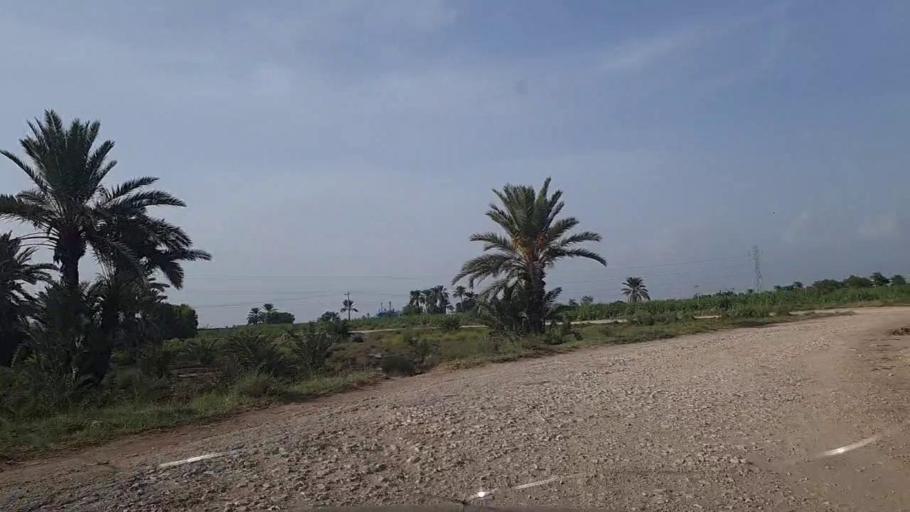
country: PK
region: Sindh
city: Ghotki
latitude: 28.0060
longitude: 69.2966
